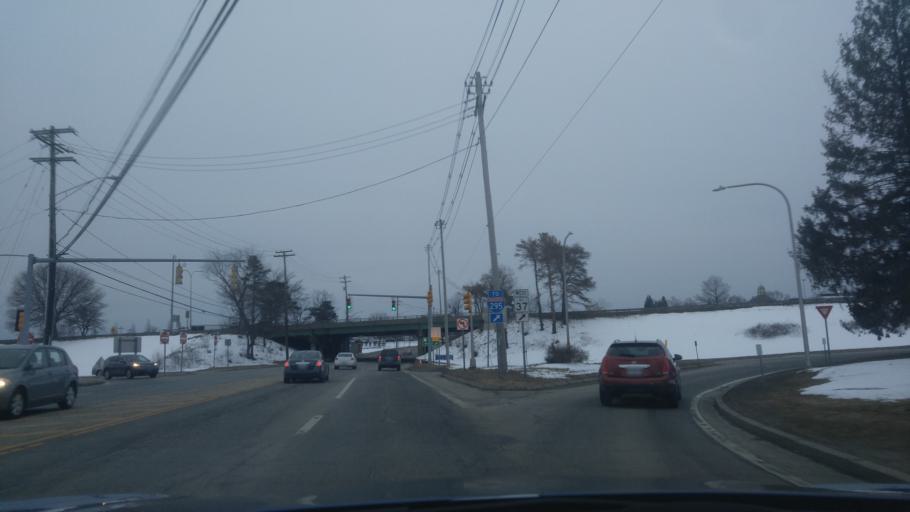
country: US
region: Rhode Island
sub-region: Providence County
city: Cranston
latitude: 41.7512
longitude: -71.4519
